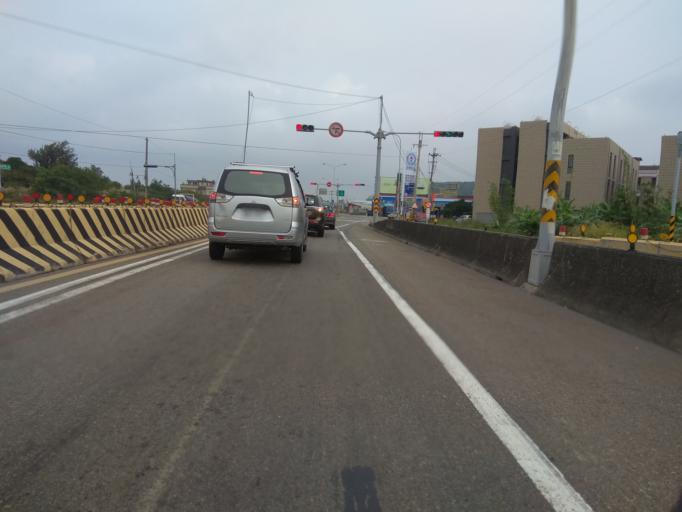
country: TW
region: Taiwan
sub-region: Hsinchu
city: Zhubei
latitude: 24.8715
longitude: 120.9538
